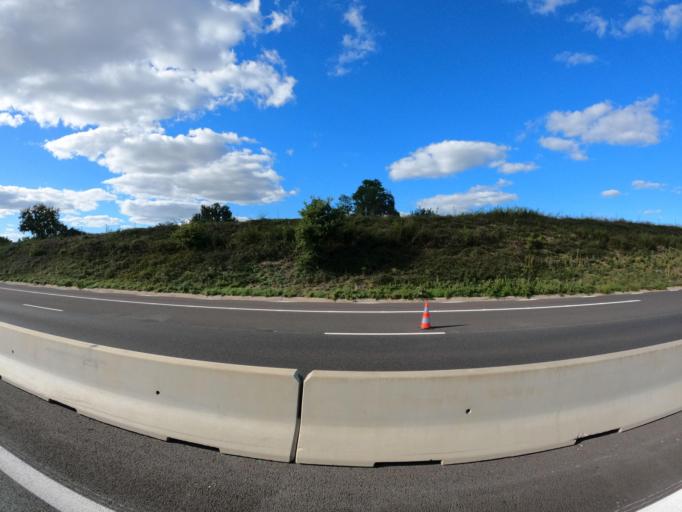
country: FR
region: Auvergne
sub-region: Departement de l'Allier
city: Molinet
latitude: 46.4585
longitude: 3.9377
